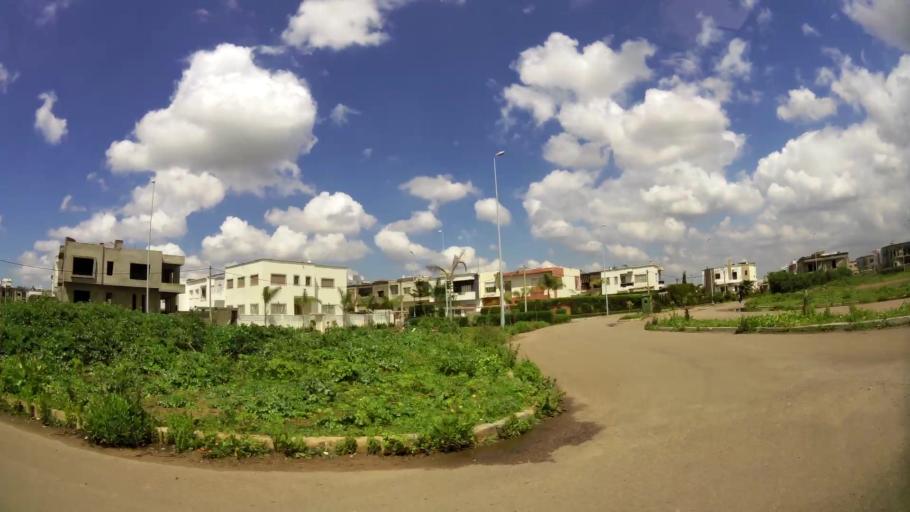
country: MA
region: Chaouia-Ouardigha
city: Nouaseur
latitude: 33.3963
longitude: -7.5637
